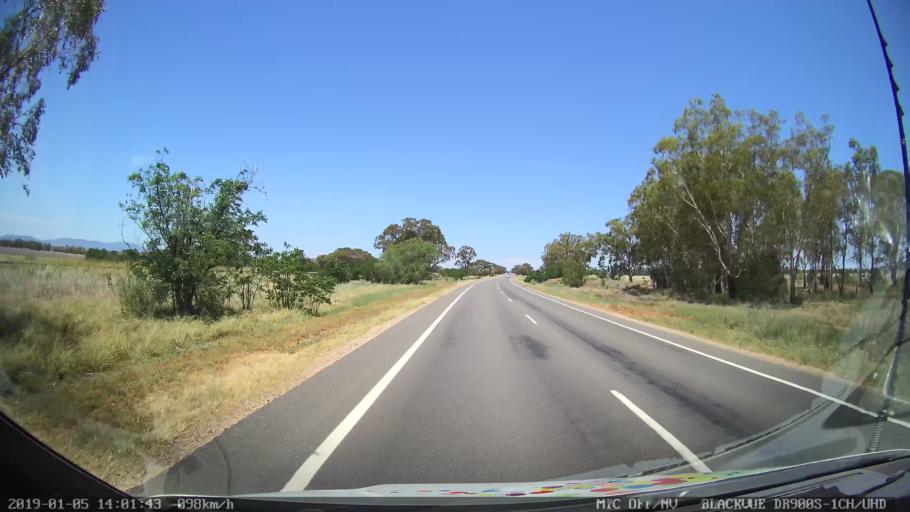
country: AU
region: New South Wales
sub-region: Gunnedah
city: Gunnedah
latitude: -31.1726
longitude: 150.3286
